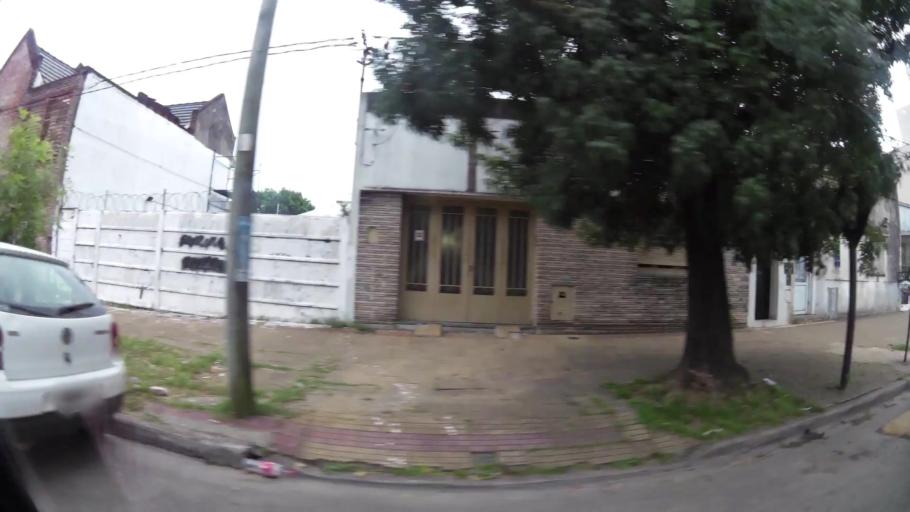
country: AR
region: Buenos Aires
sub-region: Partido de La Plata
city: La Plata
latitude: -34.9208
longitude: -57.9805
